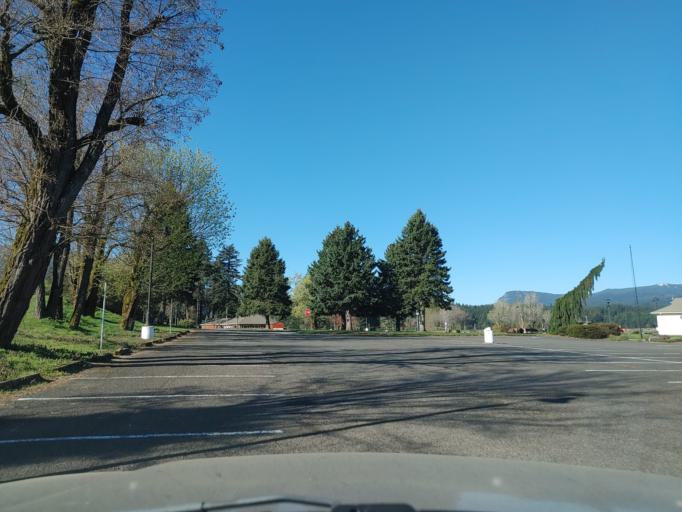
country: US
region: Oregon
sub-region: Hood River County
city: Cascade Locks
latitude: 45.6711
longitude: -121.8920
